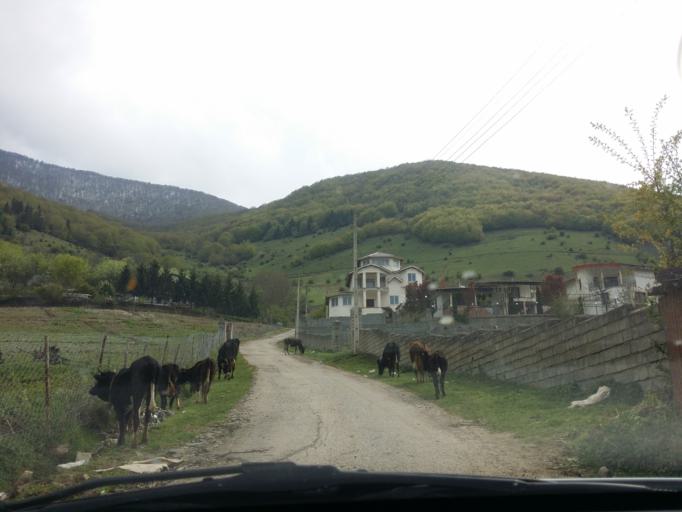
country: IR
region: Mazandaran
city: `Abbasabad
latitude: 36.4861
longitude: 51.1518
